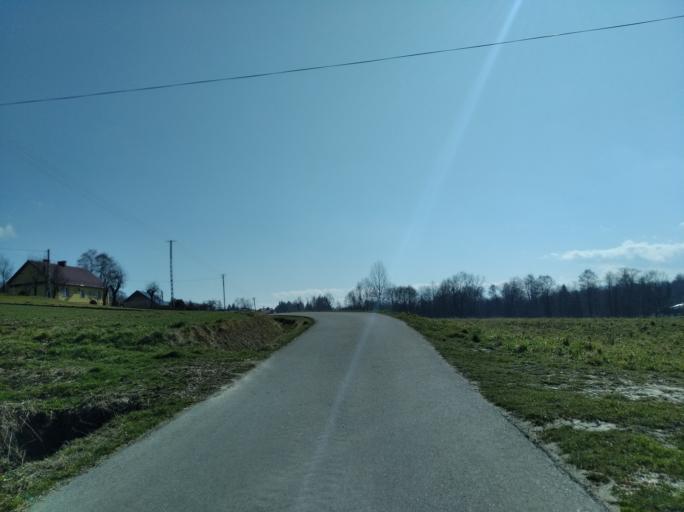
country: PL
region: Subcarpathian Voivodeship
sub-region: Powiat strzyzowski
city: Wysoka Strzyzowska
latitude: 49.8450
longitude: 21.7359
